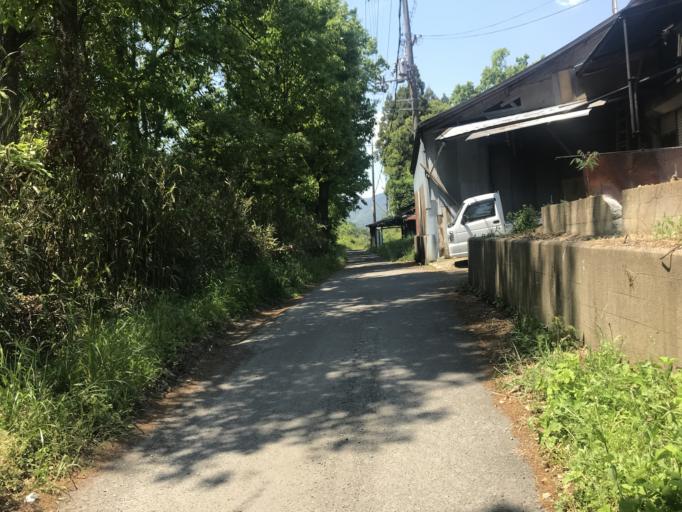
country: JP
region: Kyoto
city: Kameoka
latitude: 35.0688
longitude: 135.5704
